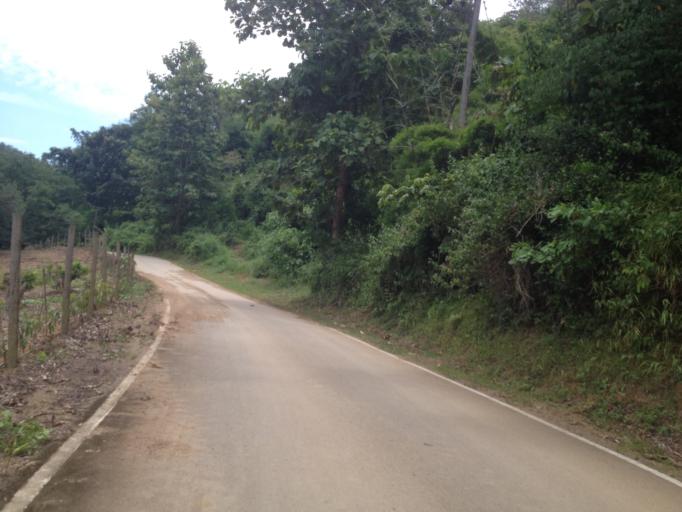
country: TH
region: Chiang Mai
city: Hang Dong
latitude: 18.7244
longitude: 98.8321
